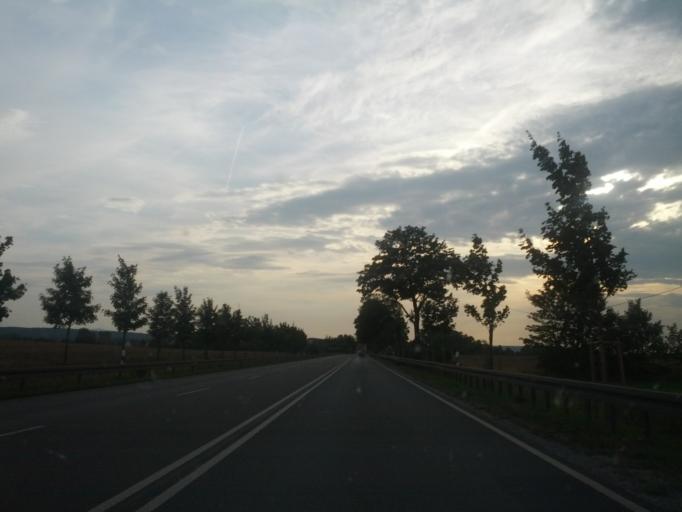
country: DE
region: Thuringia
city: Tuttleben
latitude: 50.9454
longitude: 10.8030
